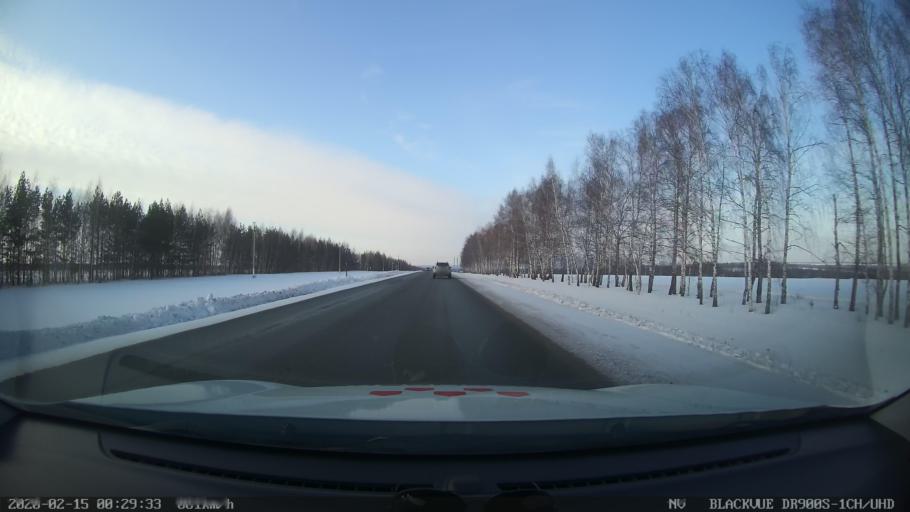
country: RU
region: Tatarstan
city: Verkhniy Uslon
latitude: 55.6517
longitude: 48.8671
